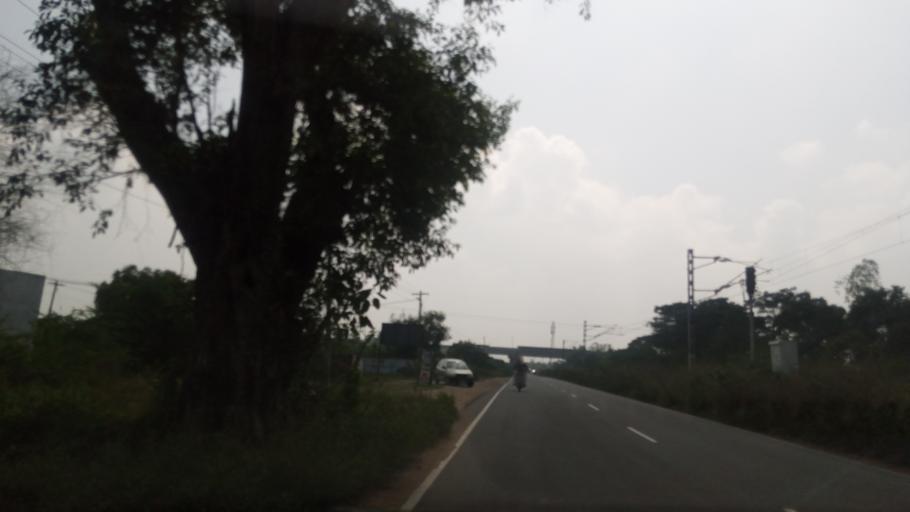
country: IN
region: Tamil Nadu
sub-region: Kancheepuram
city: Kanchipuram
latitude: 12.8772
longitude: 79.6899
